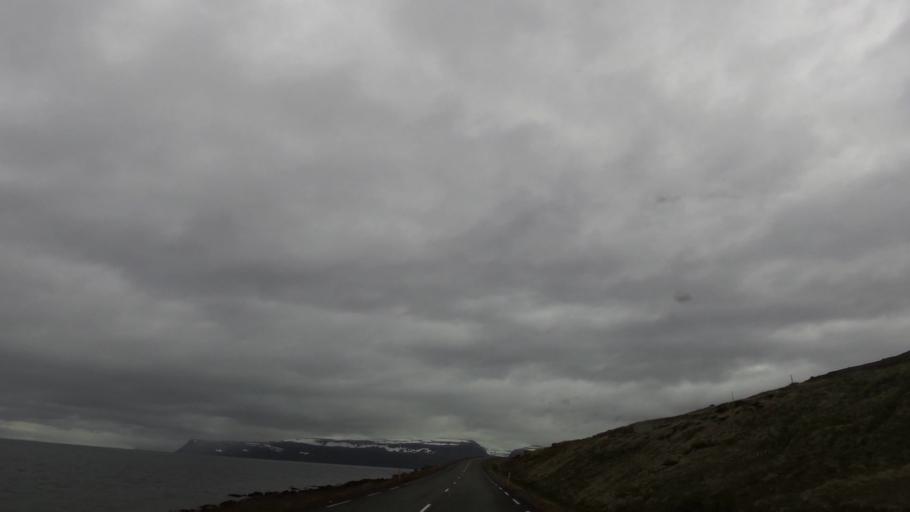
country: IS
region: Westfjords
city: Isafjoerdur
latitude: 66.0427
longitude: -22.7714
